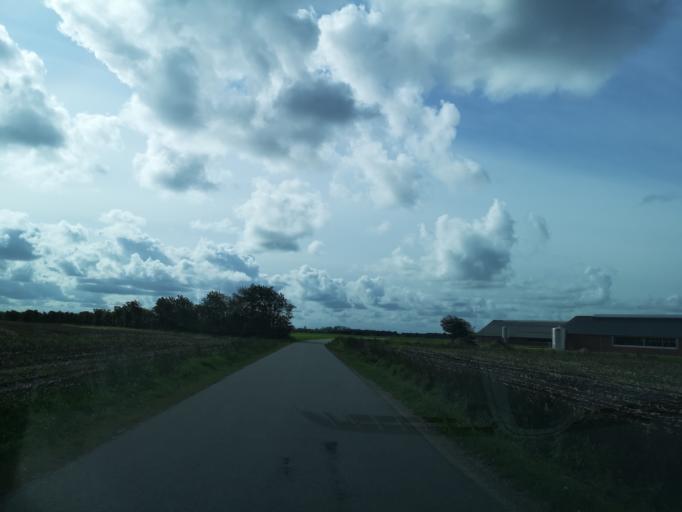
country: DK
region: Central Jutland
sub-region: Ringkobing-Skjern Kommune
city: Tarm
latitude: 55.9524
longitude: 8.5506
